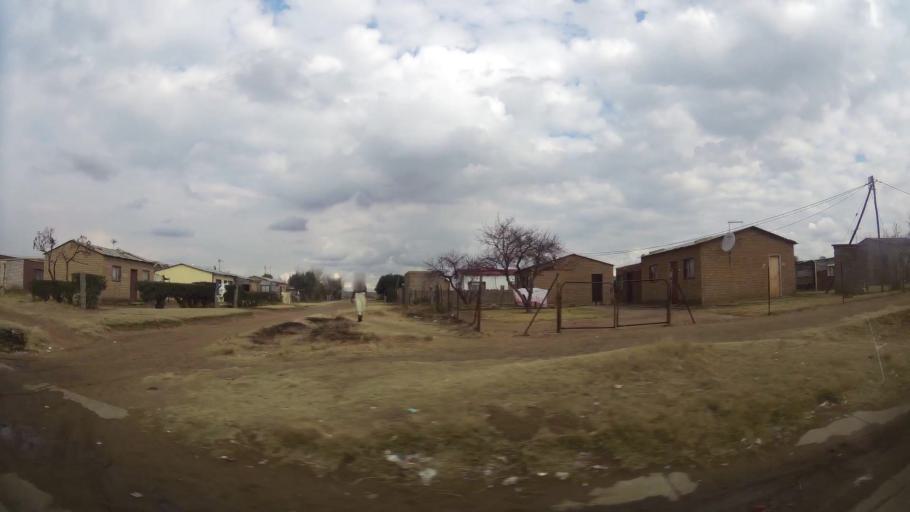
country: ZA
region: Orange Free State
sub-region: Fezile Dabi District Municipality
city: Sasolburg
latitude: -26.8623
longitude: 27.8569
